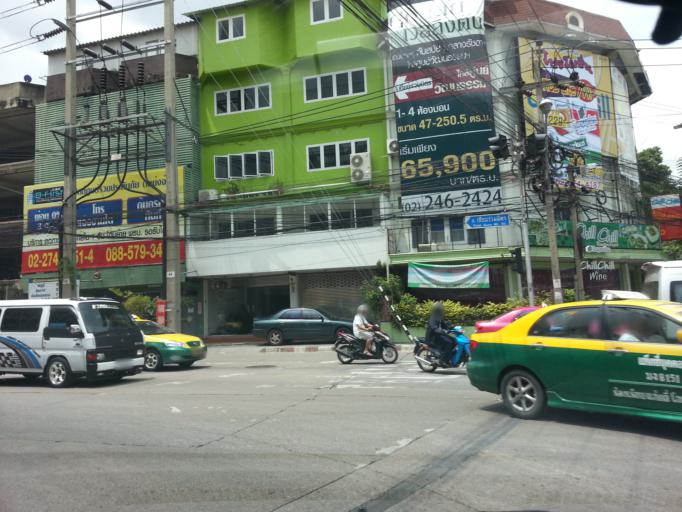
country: TH
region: Bangkok
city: Huai Khwang
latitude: 13.7698
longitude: 100.5866
